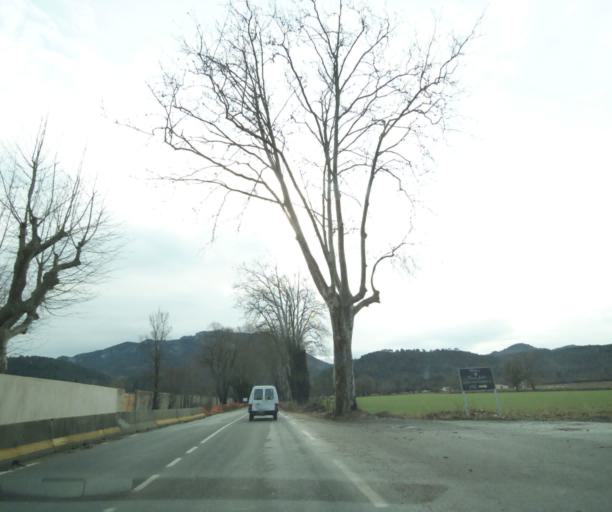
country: FR
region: Provence-Alpes-Cote d'Azur
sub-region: Departement du Var
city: Tourves
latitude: 43.3939
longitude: 5.9745
